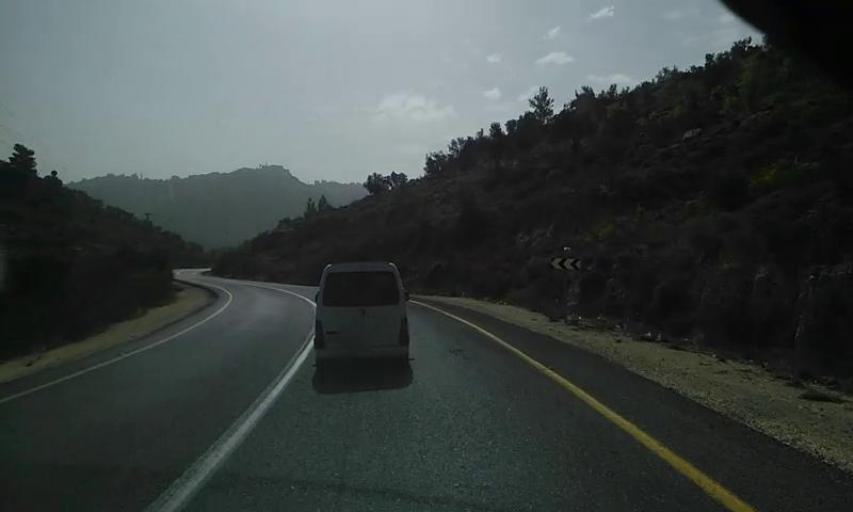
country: PS
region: West Bank
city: Silwad
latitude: 31.9952
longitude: 35.2424
